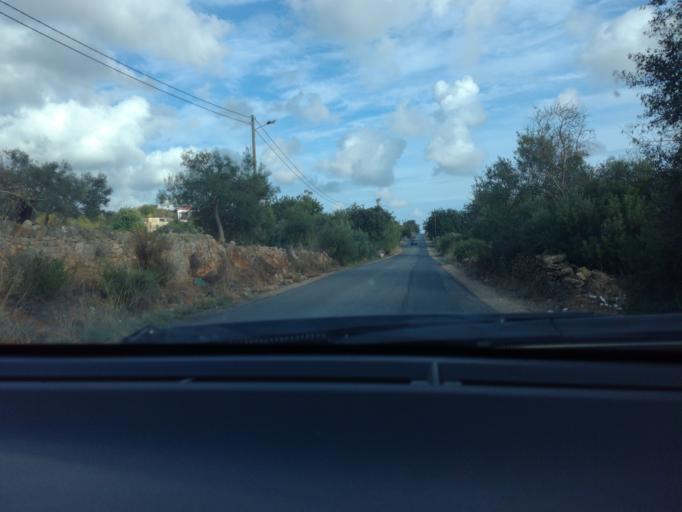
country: PT
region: Faro
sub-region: Olhao
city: Olhao
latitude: 37.0849
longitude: -7.8773
